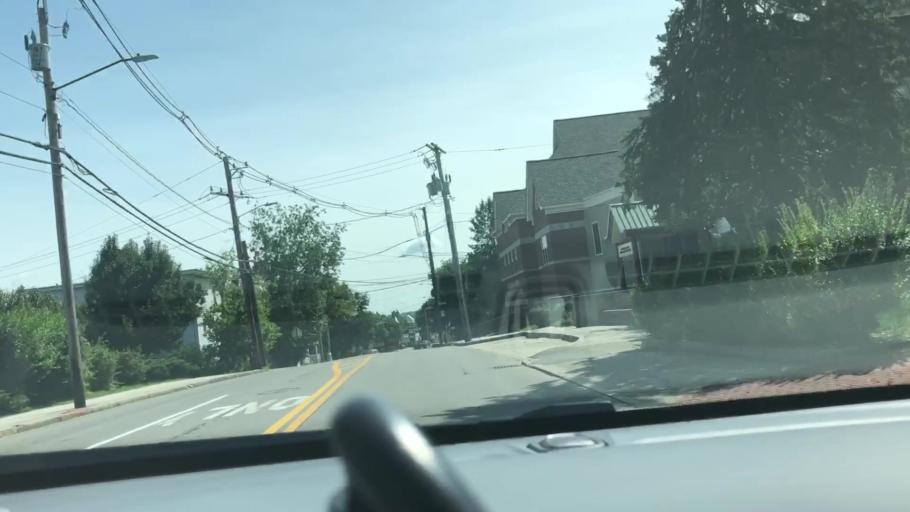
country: US
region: New Hampshire
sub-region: Hillsborough County
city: Manchester
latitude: 42.9854
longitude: -71.4740
